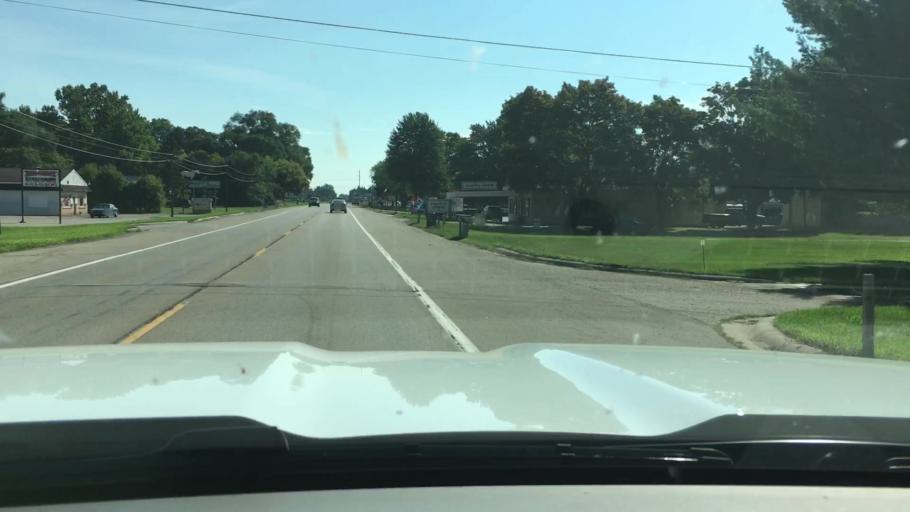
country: US
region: Michigan
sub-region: Gratiot County
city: Alma
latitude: 43.4079
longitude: -84.6423
